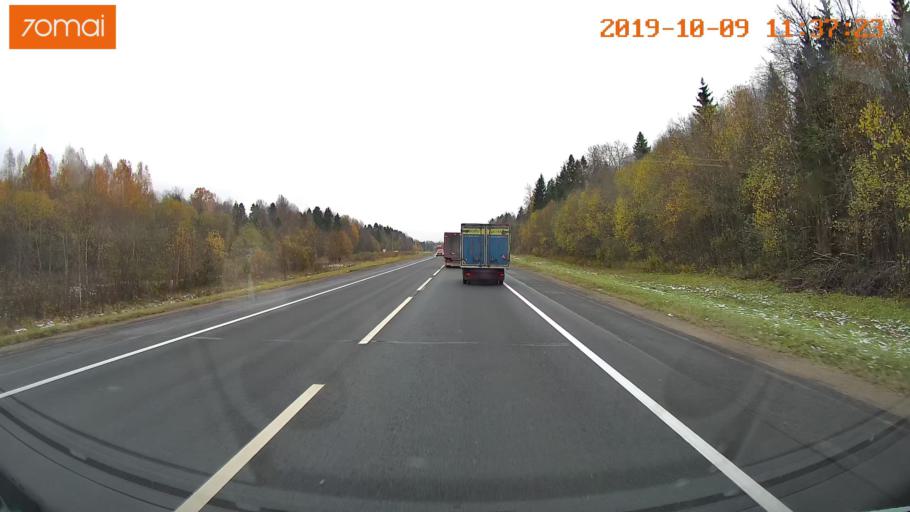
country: RU
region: Vologda
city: Gryazovets
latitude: 58.9799
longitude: 40.1458
